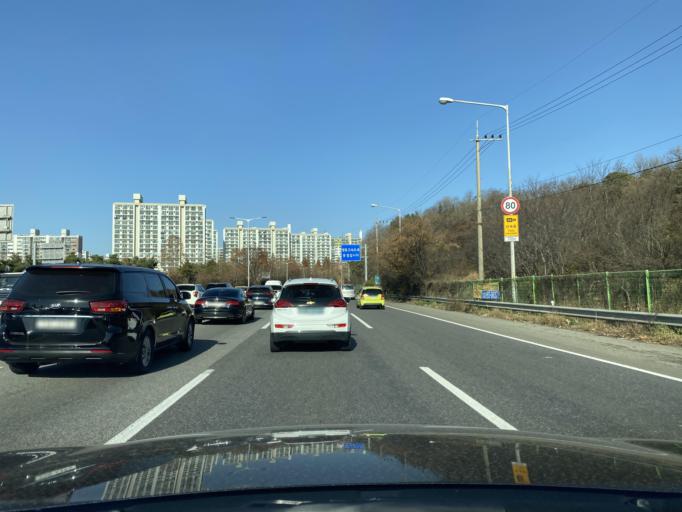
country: KR
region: Incheon
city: Incheon
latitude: 37.4371
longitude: 126.7396
